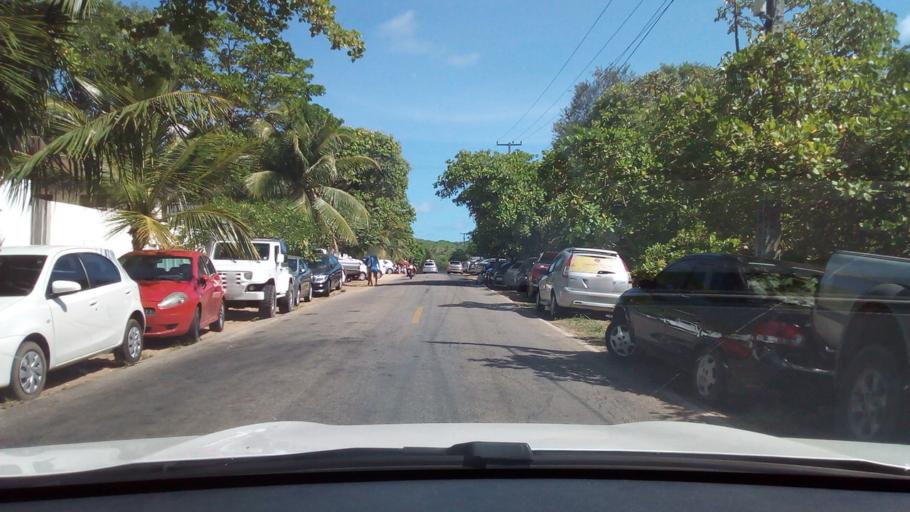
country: BR
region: Rio Grande do Norte
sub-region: Ares
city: Ares
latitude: -6.2234
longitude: -35.0712
